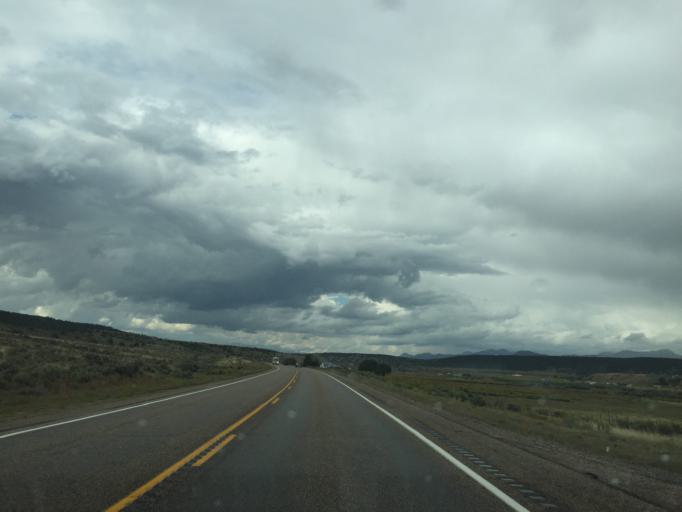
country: US
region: Utah
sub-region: Garfield County
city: Panguitch
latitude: 37.7330
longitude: -112.3798
